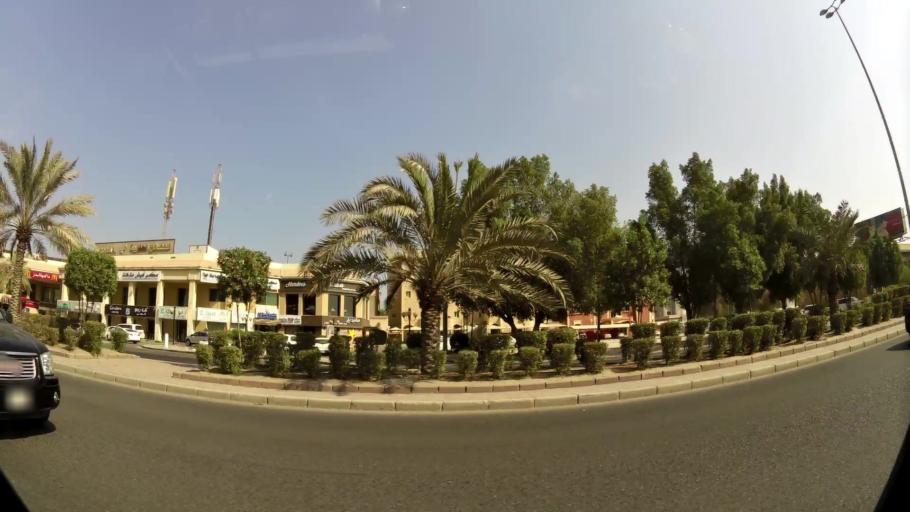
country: KW
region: Al Ahmadi
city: Al Mahbulah
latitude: 29.1428
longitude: 48.1289
